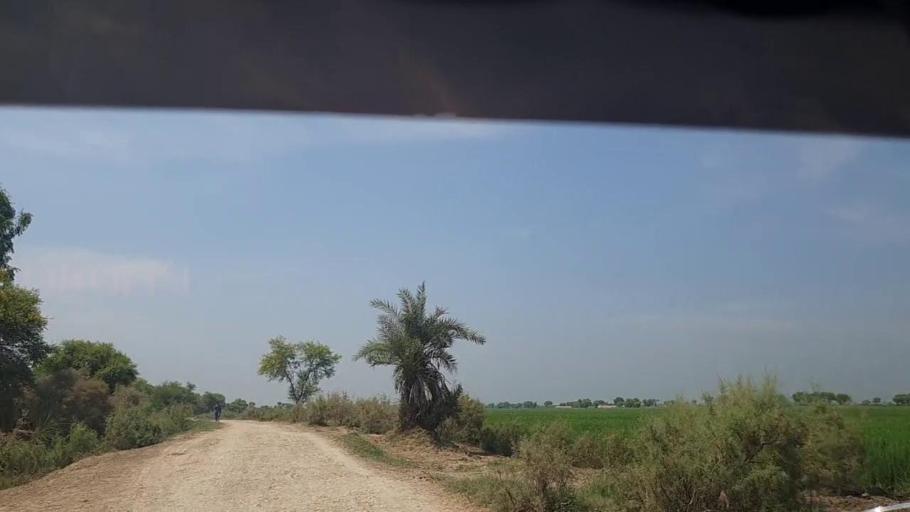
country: PK
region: Sindh
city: Thul
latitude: 28.1917
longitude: 68.7124
